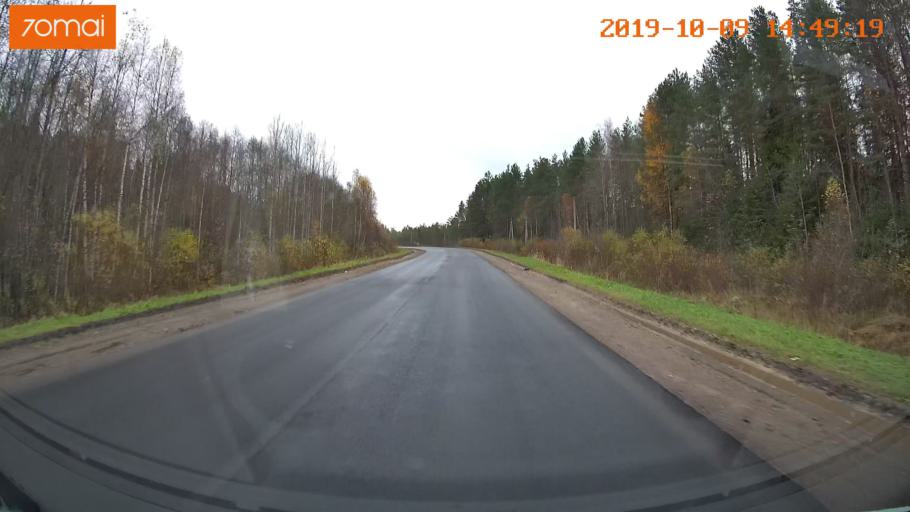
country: RU
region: Kostroma
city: Chistyye Bory
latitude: 58.3946
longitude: 41.5808
